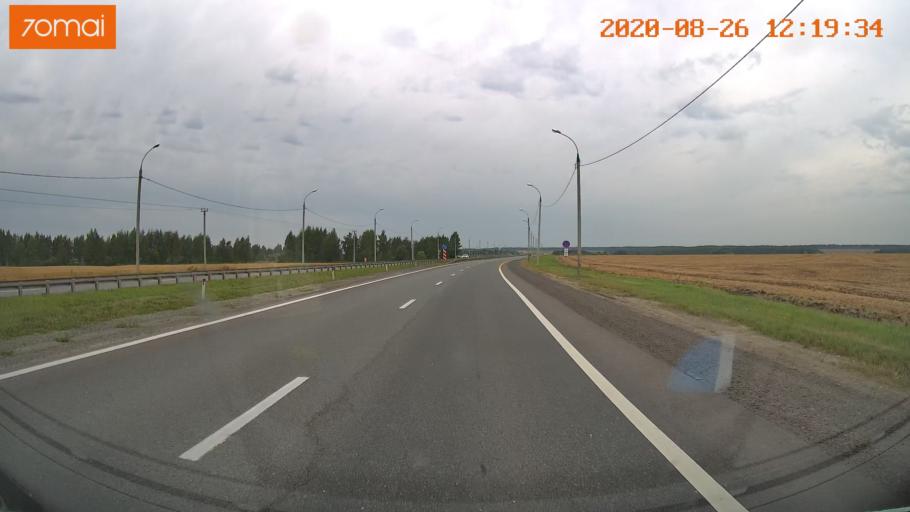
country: RU
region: Rjazan
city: Murmino
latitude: 54.4766
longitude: 39.9946
